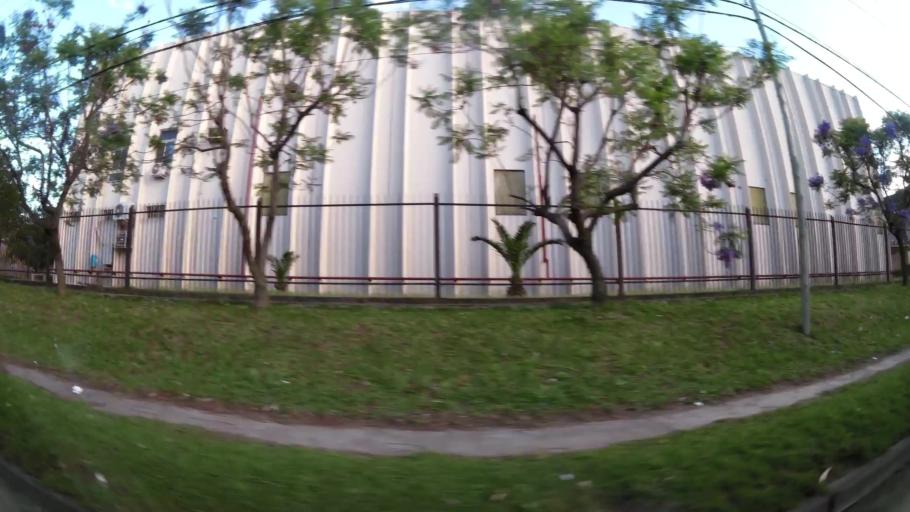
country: AR
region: Buenos Aires
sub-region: Partido de Tigre
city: Tigre
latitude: -34.4699
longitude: -58.5635
